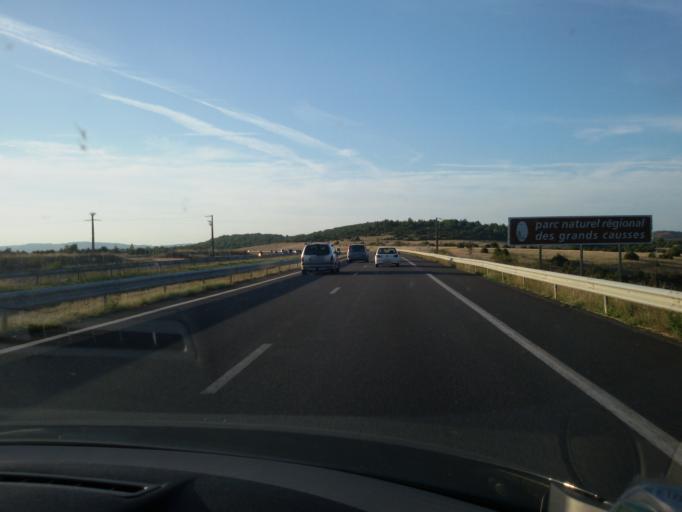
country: FR
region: Midi-Pyrenees
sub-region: Departement de l'Aveyron
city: La Cavalerie
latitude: 43.9147
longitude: 3.2536
